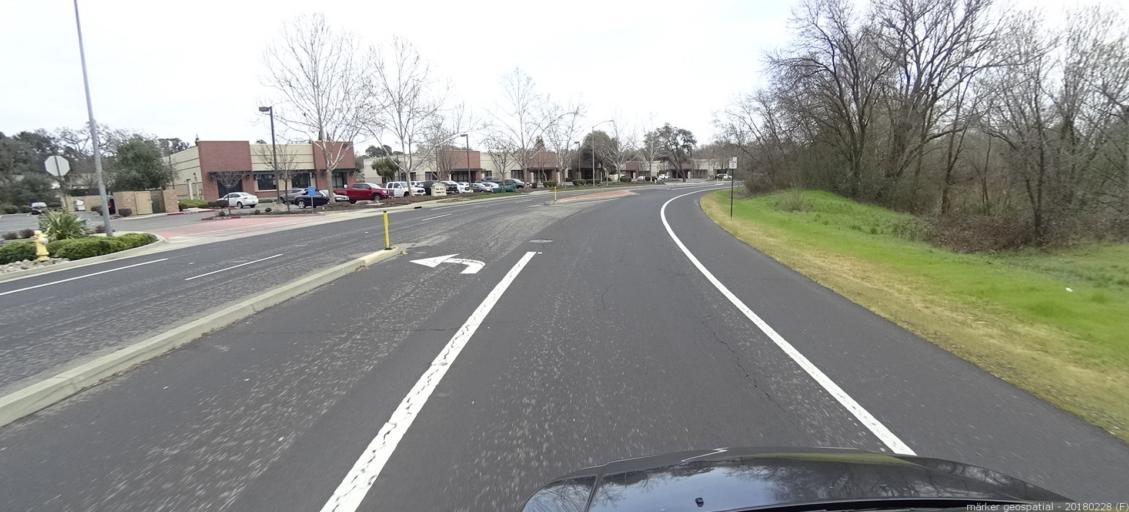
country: US
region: California
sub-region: Sacramento County
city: Folsom
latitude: 38.6640
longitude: -121.1777
